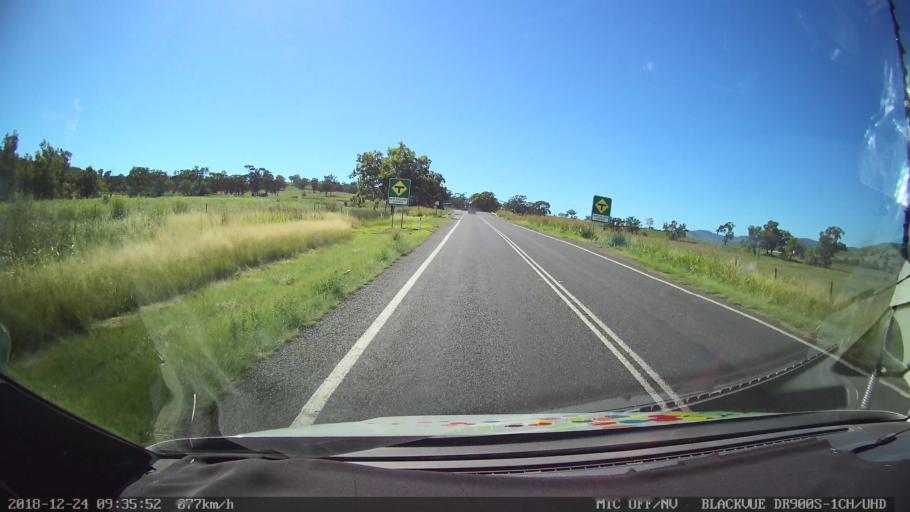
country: AU
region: New South Wales
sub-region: Liverpool Plains
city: Quirindi
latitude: -31.6326
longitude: 150.7190
